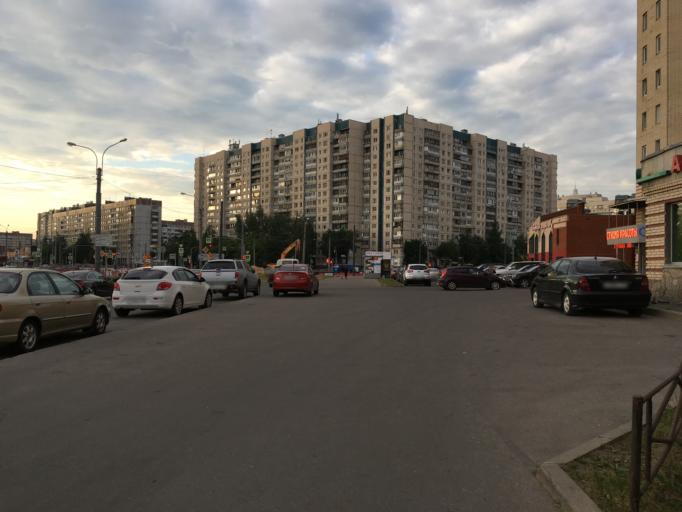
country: RU
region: St.-Petersburg
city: Staraya Derevnya
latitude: 60.0071
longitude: 30.2486
